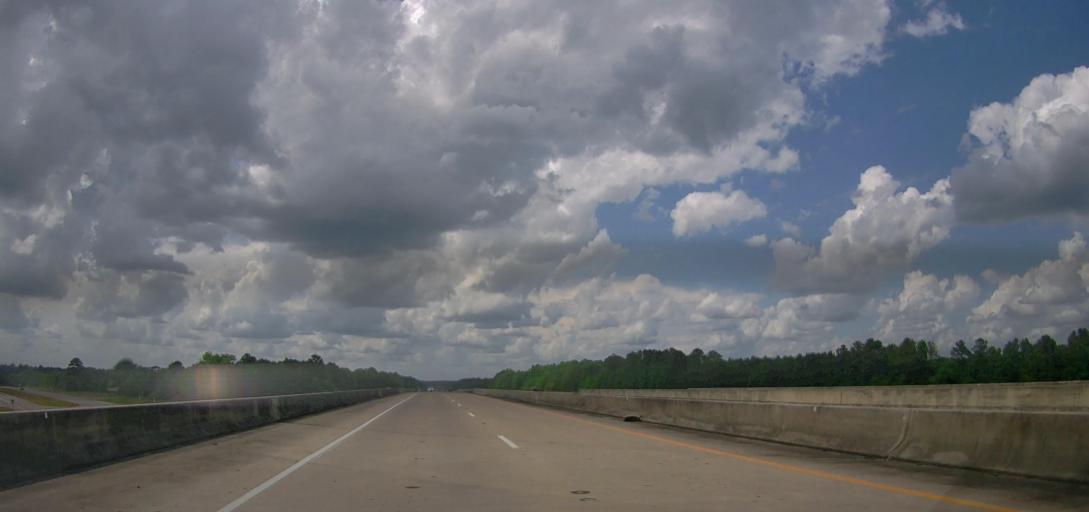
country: US
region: Alabama
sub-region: Walker County
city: Carbon Hill
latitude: 33.8696
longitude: -87.4386
